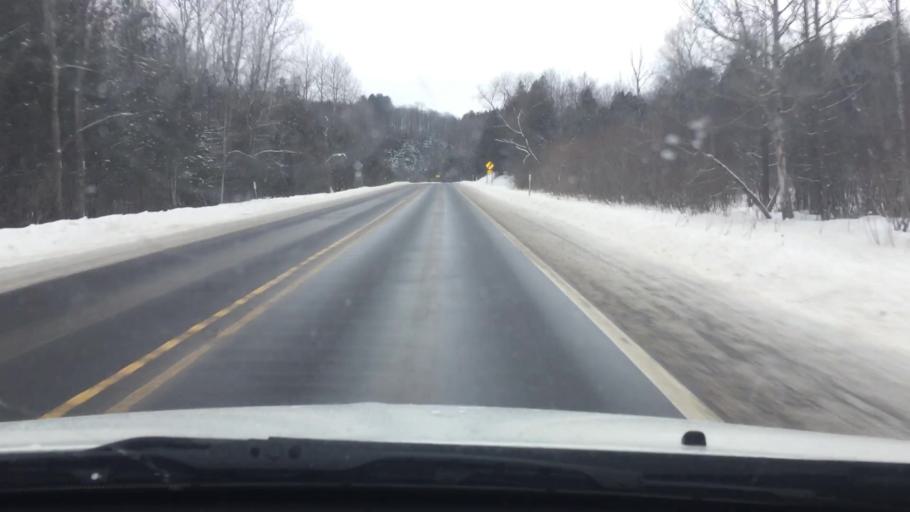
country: US
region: Michigan
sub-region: Charlevoix County
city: East Jordan
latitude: 45.1284
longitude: -85.0756
